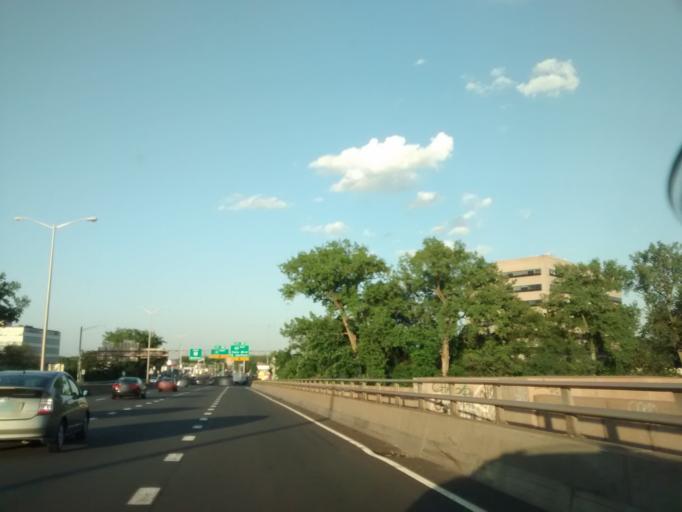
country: US
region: Connecticut
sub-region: Hartford County
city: Hartford
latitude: 41.7694
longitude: -72.6649
